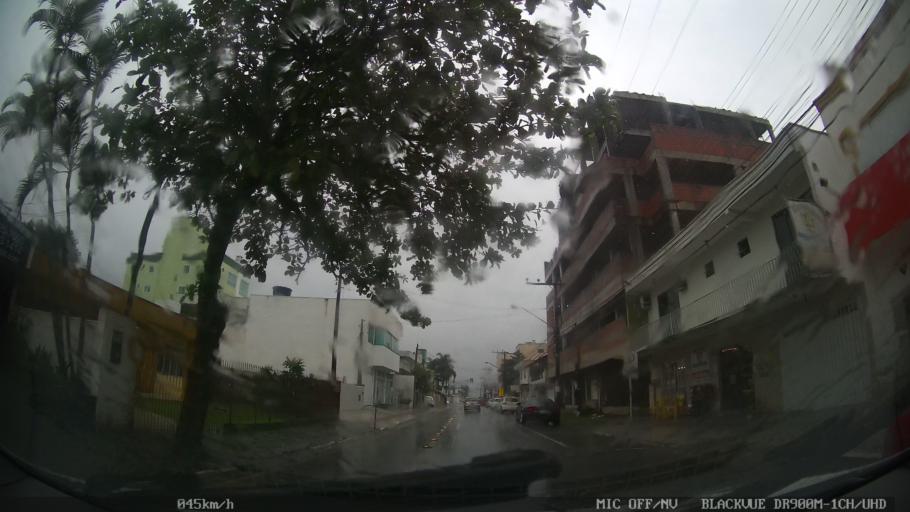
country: BR
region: Santa Catarina
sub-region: Balneario Camboriu
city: Balneario Camboriu
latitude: -27.0085
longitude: -48.6314
